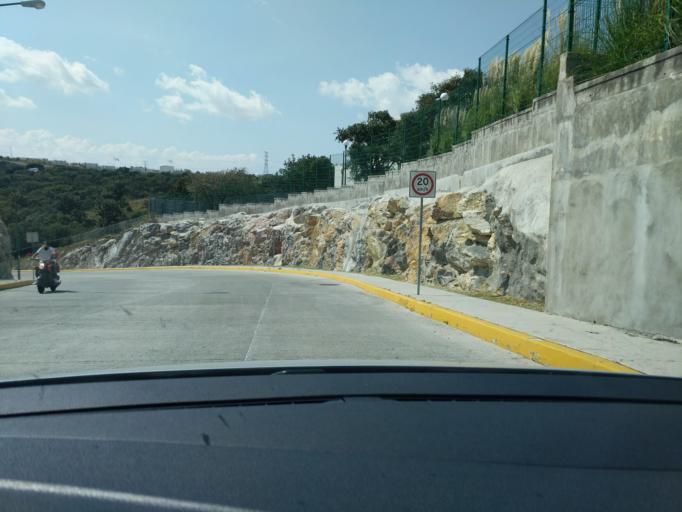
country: MX
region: Puebla
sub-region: Puebla
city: Galaxia la Calera
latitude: 19.0074
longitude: -98.1445
